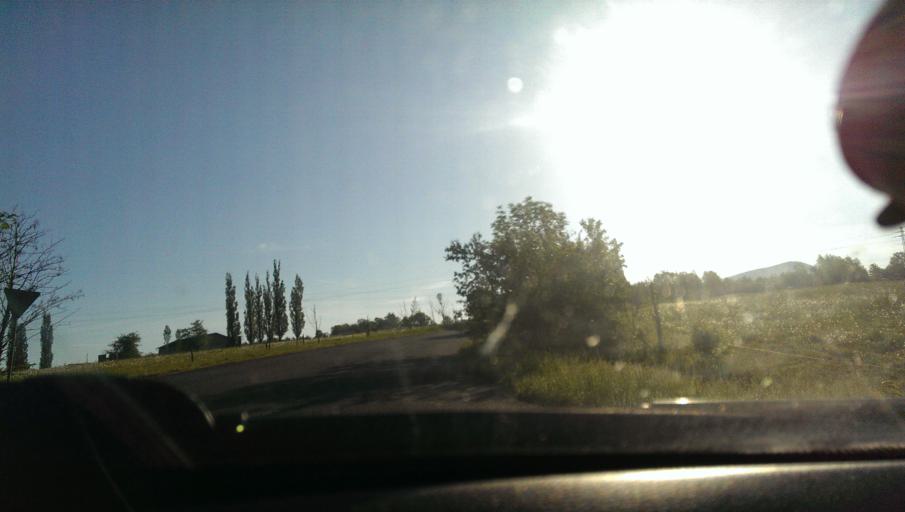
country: CZ
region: Moravskoslezsky
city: Frenstat pod Radhostem
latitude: 49.5543
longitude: 18.2178
